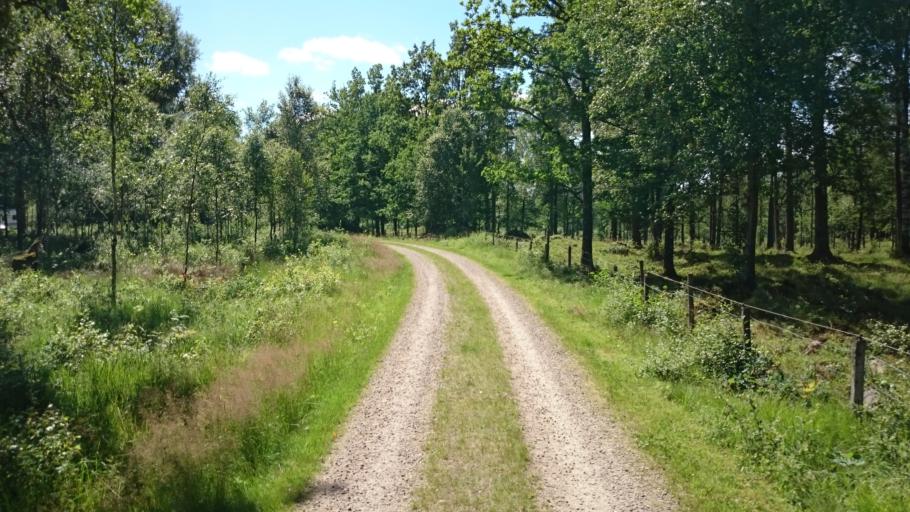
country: SE
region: Halland
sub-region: Hylte Kommun
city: Hyltebruk
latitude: 56.9750
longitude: 13.1684
